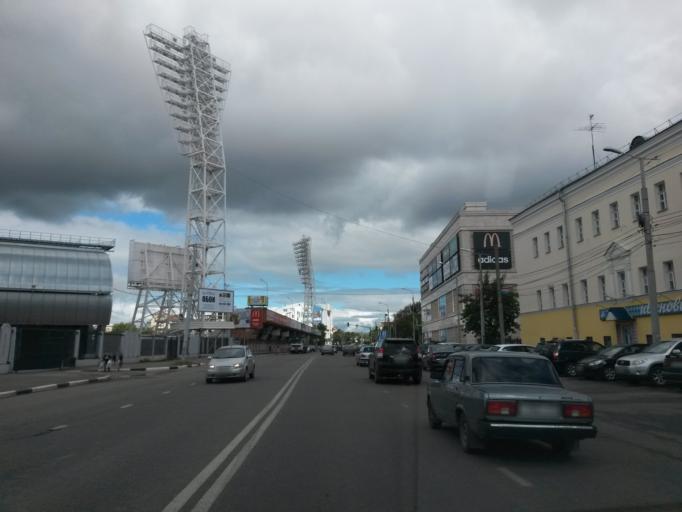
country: RU
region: Jaroslavl
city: Yaroslavl
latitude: 57.6270
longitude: 39.8682
